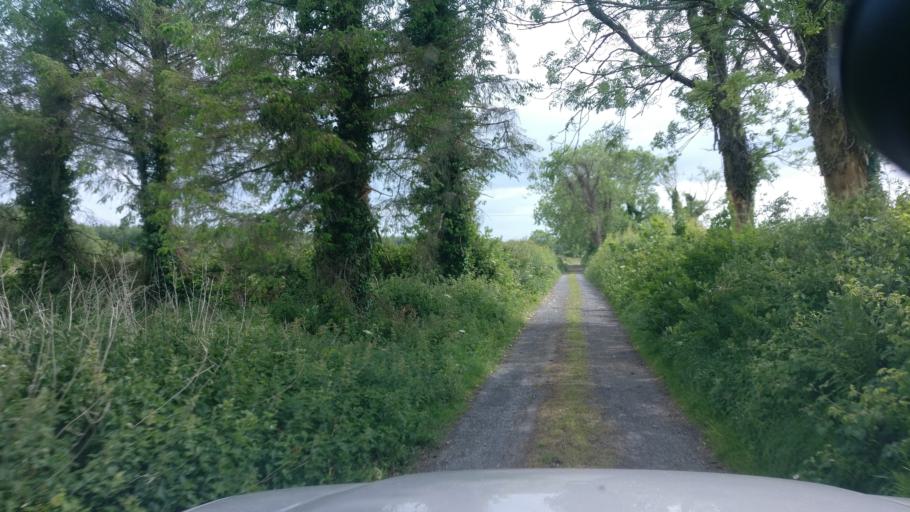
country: IE
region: Connaught
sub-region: County Galway
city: Ballinasloe
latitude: 53.2694
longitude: -8.3322
